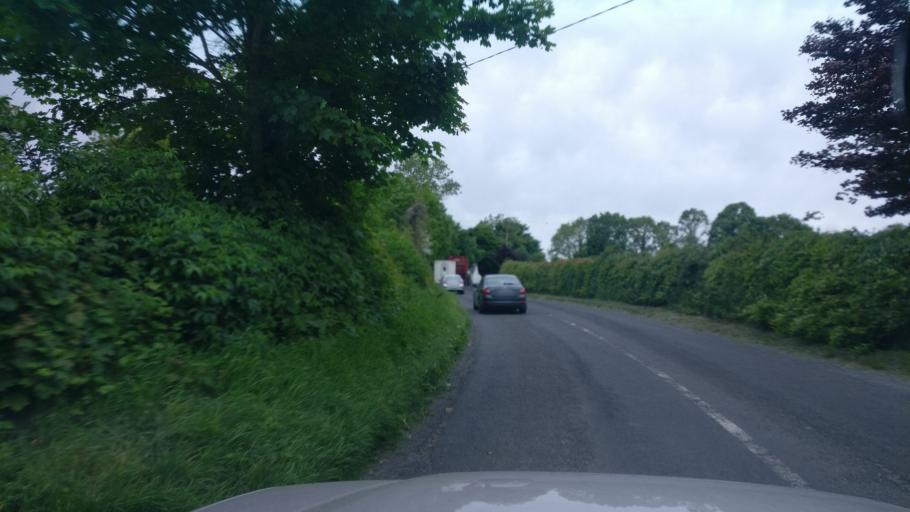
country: IE
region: Connaught
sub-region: County Galway
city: Portumna
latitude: 53.1193
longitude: -8.3143
